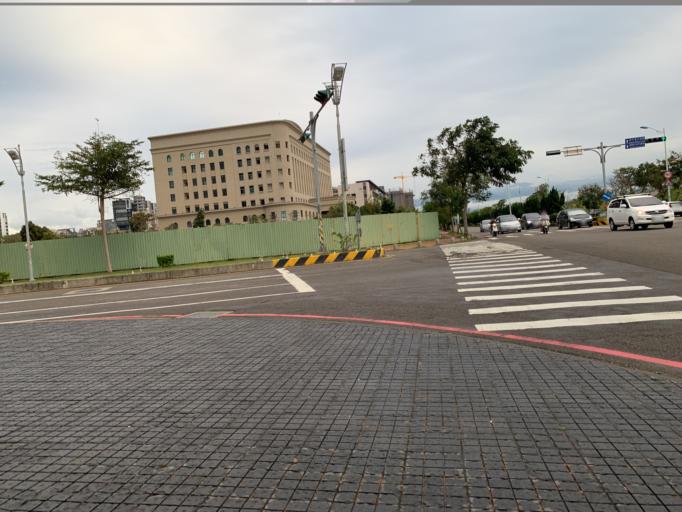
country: TW
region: Taiwan
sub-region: Hsinchu
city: Zhubei
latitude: 24.8144
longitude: 121.0161
